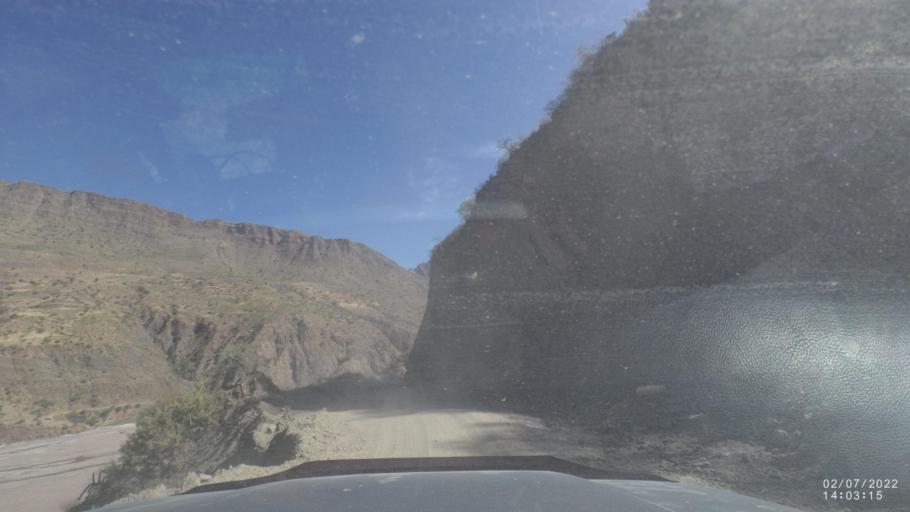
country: BO
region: Cochabamba
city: Irpa Irpa
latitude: -17.8225
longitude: -66.3898
